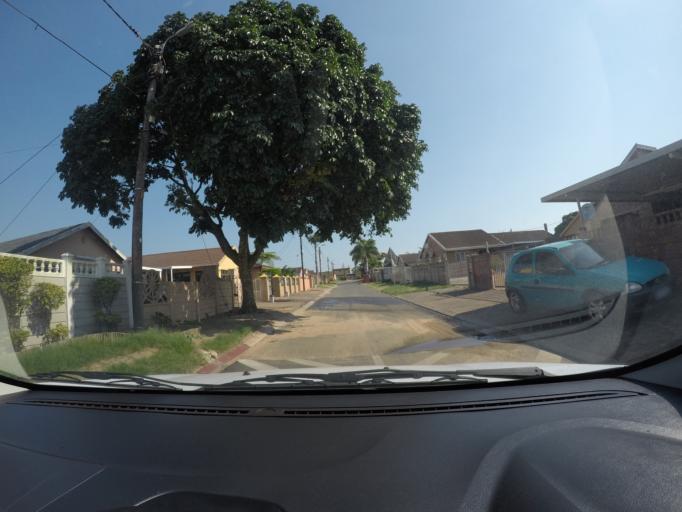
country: ZA
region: KwaZulu-Natal
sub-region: uThungulu District Municipality
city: Richards Bay
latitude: -28.7192
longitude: 32.0448
